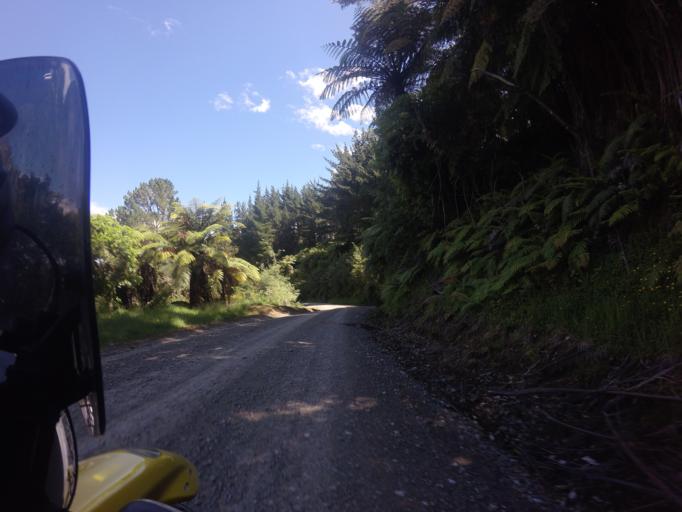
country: NZ
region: Hawke's Bay
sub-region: Wairoa District
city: Wairoa
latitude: -38.9805
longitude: 177.7034
